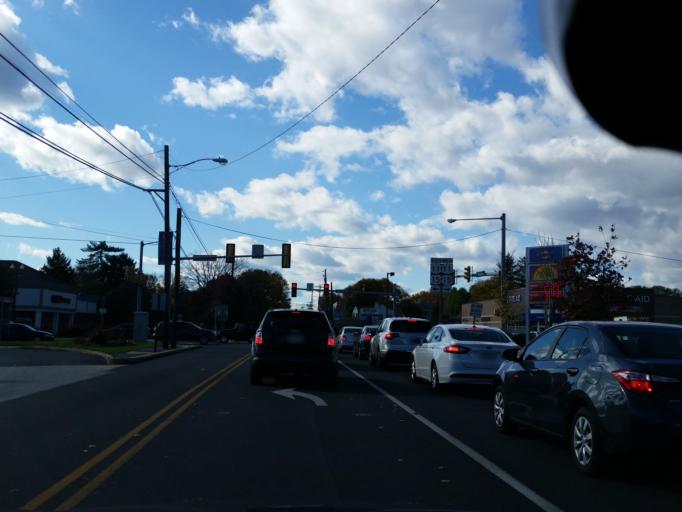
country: US
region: Pennsylvania
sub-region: Cumberland County
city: Camp Hill
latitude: 40.2399
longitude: -76.9339
